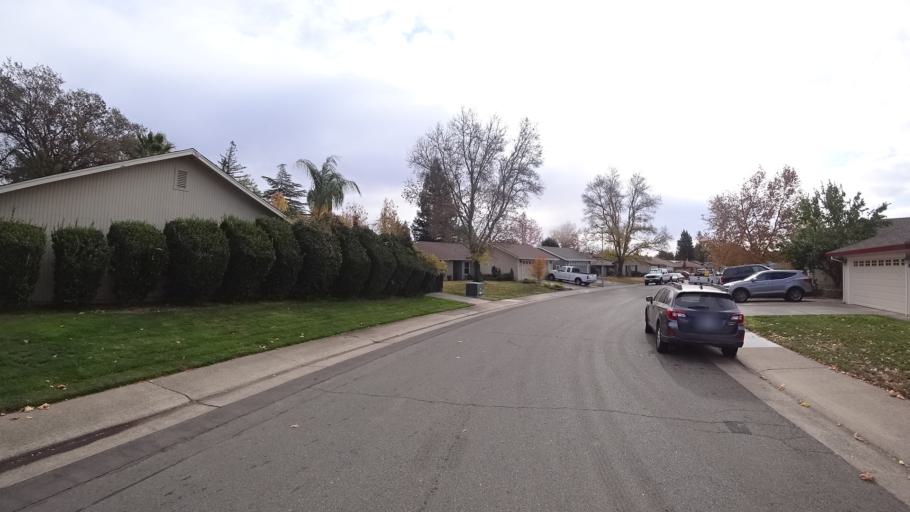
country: US
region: California
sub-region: Sacramento County
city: Citrus Heights
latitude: 38.7145
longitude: -121.2471
